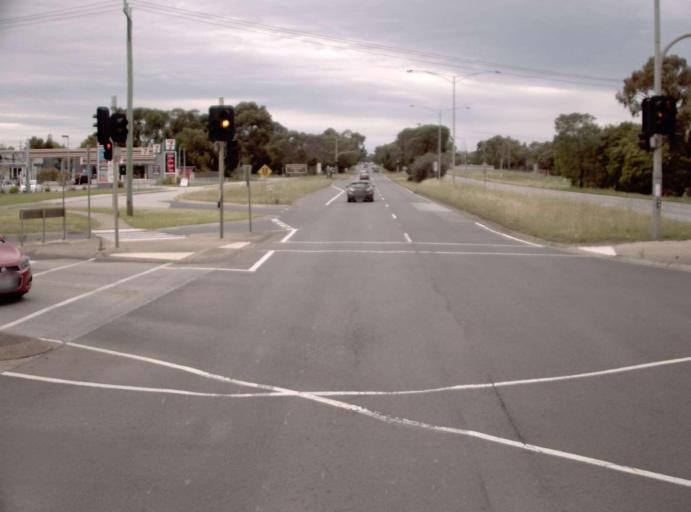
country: AU
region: Victoria
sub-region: Casey
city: Cranbourne North
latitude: -38.0740
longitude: 145.2714
